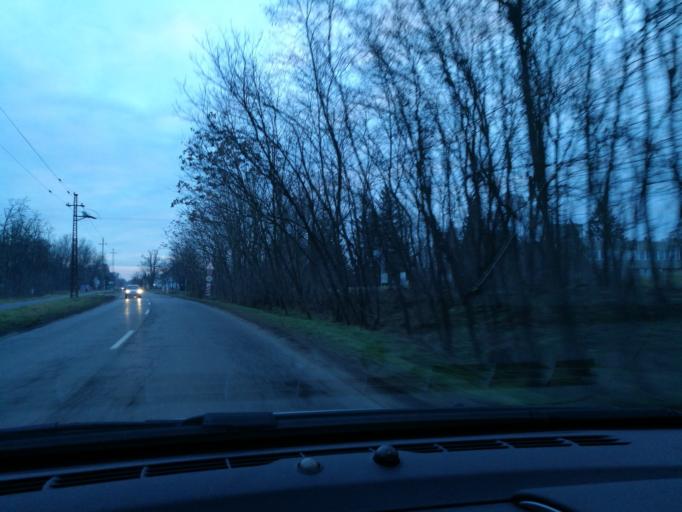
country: HU
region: Szabolcs-Szatmar-Bereg
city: Nyiregyhaza
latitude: 47.9784
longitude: 21.7052
